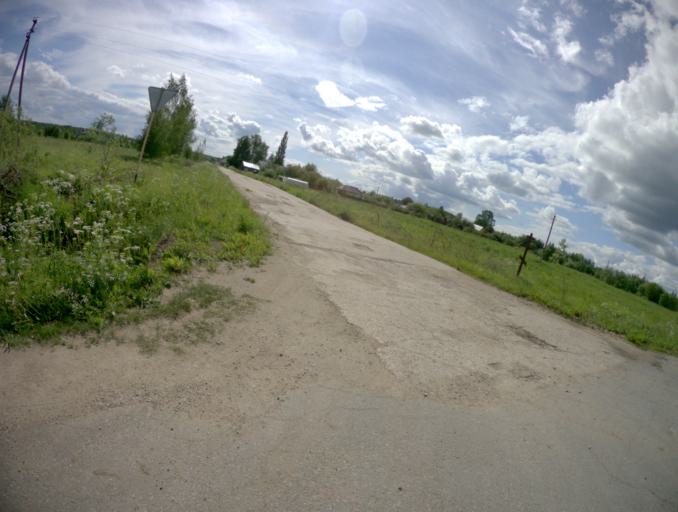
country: RU
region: Vladimir
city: Yur'yev-Pol'skiy
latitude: 56.3148
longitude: 39.7873
